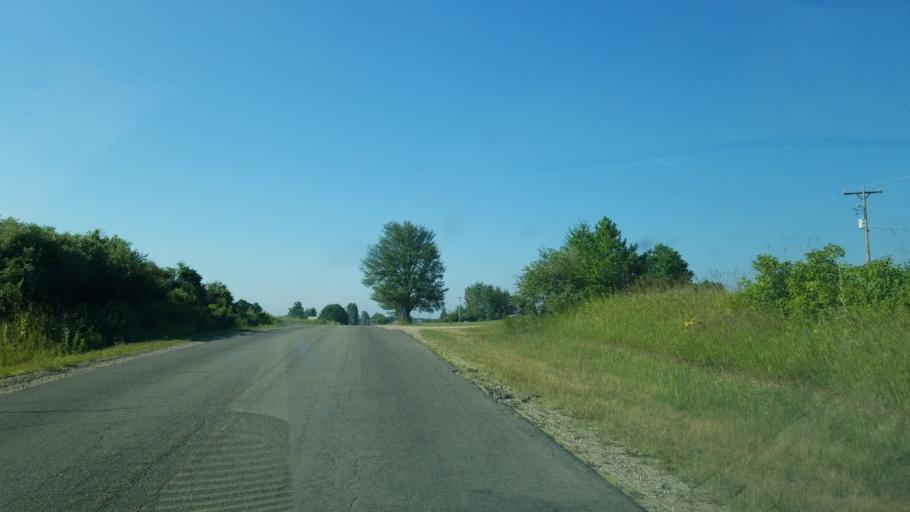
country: US
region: Michigan
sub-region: Mecosta County
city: Canadian Lakes
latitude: 43.4956
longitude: -85.3928
